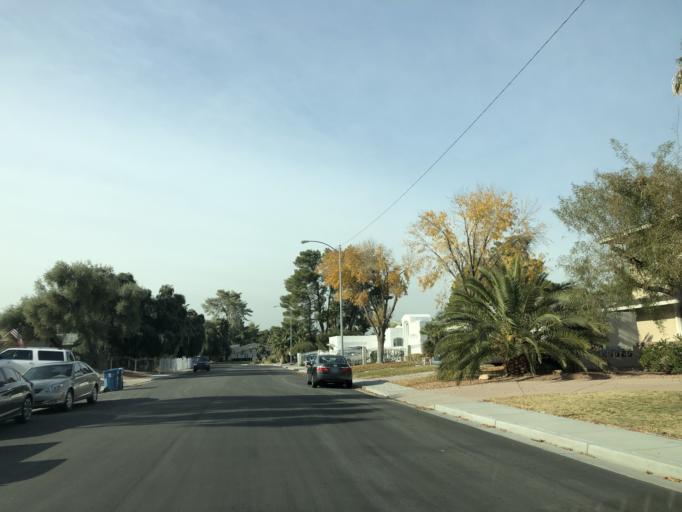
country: US
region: Nevada
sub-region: Clark County
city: Winchester
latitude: 36.1244
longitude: -115.1224
